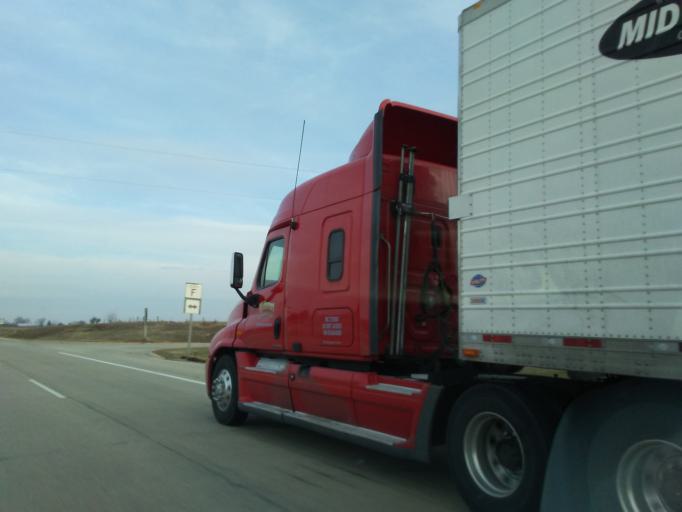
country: US
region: Wisconsin
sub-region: Iowa County
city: Barneveld
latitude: 43.0103
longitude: -89.8250
